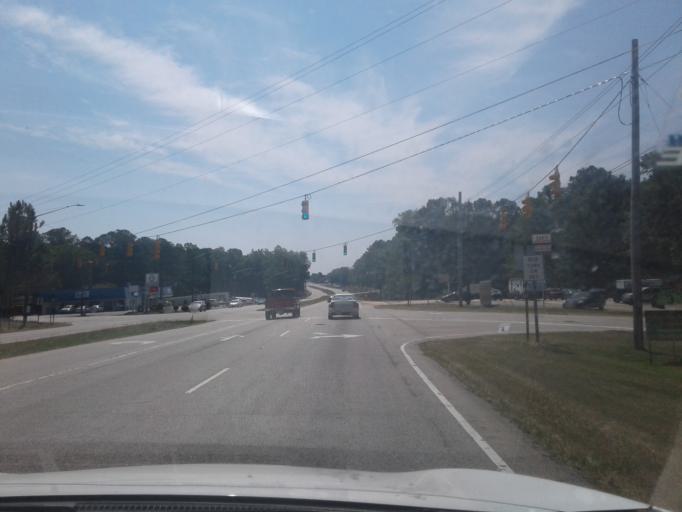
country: US
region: North Carolina
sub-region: Harnett County
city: Erwin
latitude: 35.3355
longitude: -78.6741
